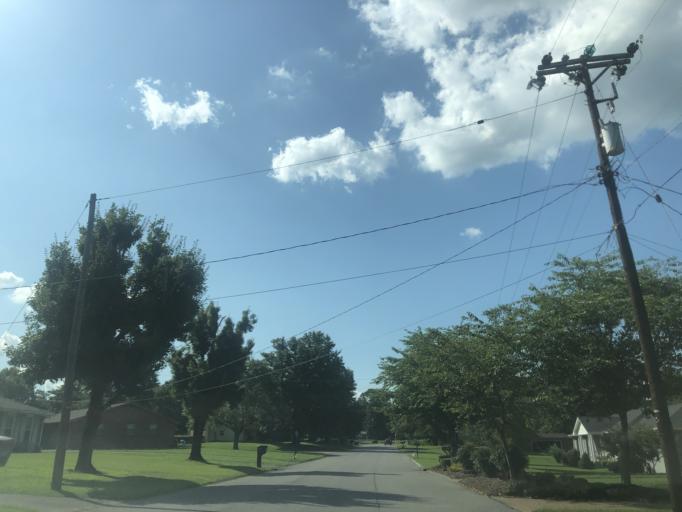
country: US
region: Tennessee
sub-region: Davidson County
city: Lakewood
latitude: 36.2091
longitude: -86.5987
